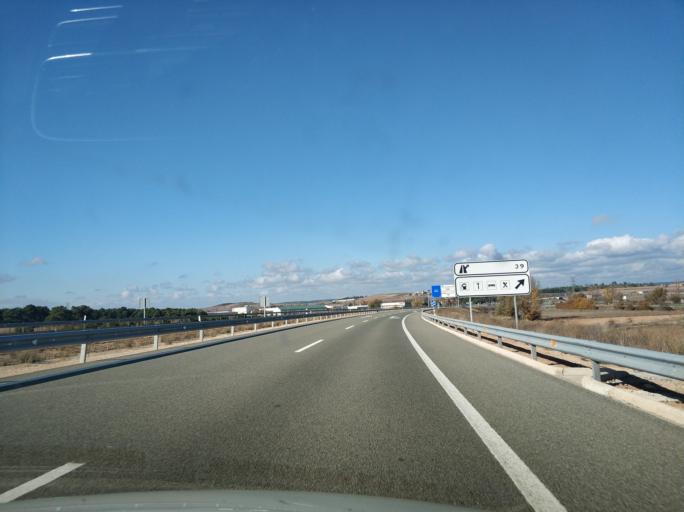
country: ES
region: Castille and Leon
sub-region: Provincia de Soria
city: Almazan
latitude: 41.4635
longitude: -2.5223
